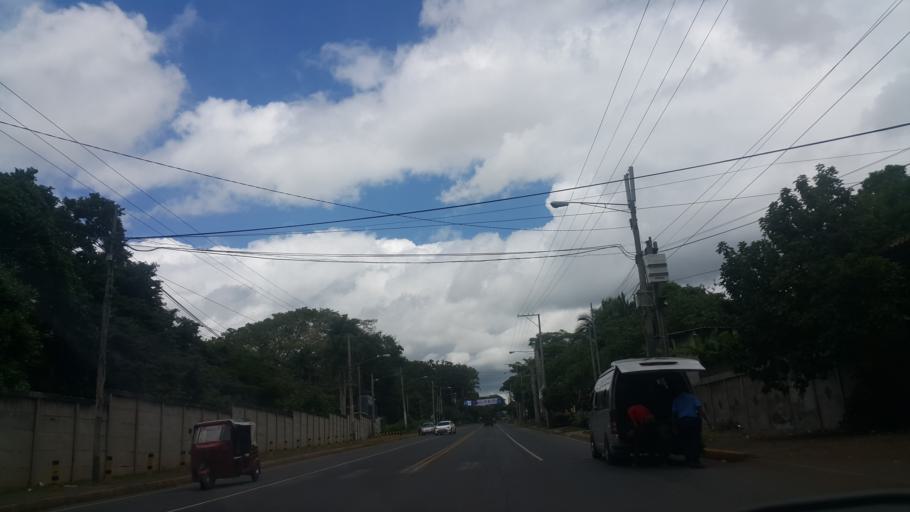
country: NI
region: Managua
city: Ciudad Sandino
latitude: 12.0871
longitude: -86.3238
